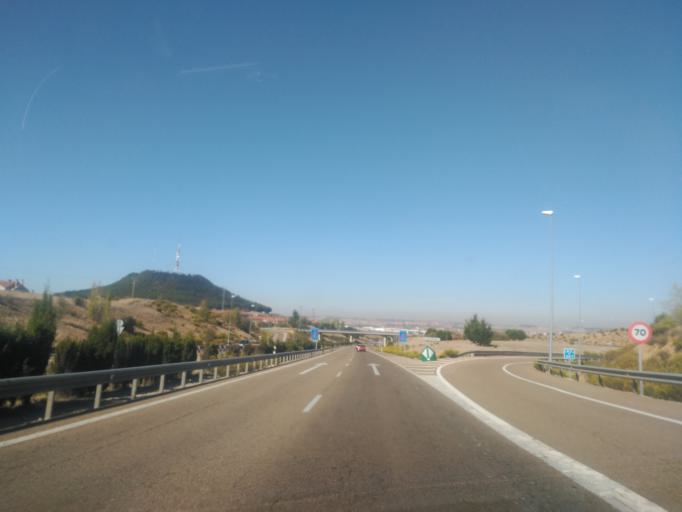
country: ES
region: Castille and Leon
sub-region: Provincia de Valladolid
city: Cisterniga
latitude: 41.6160
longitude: -4.6810
